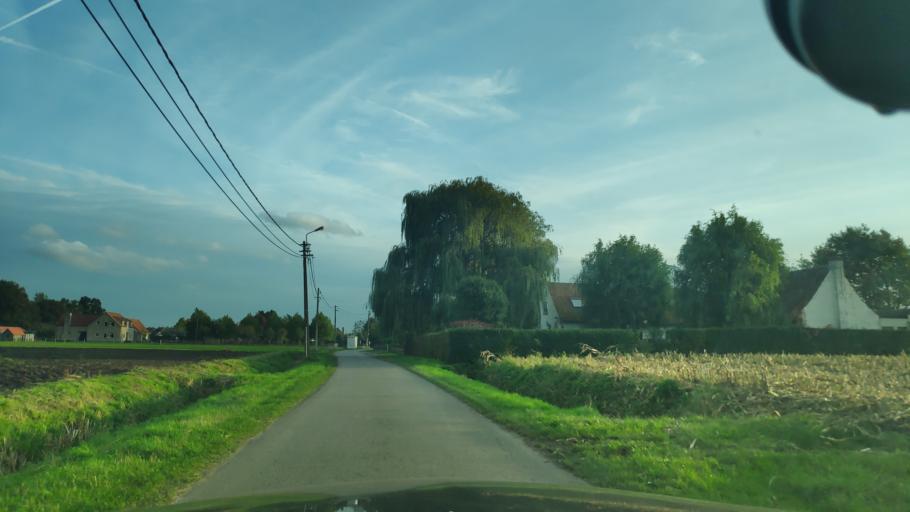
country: BE
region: Flanders
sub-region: Provincie Oost-Vlaanderen
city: Aalter
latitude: 51.1201
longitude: 3.4440
